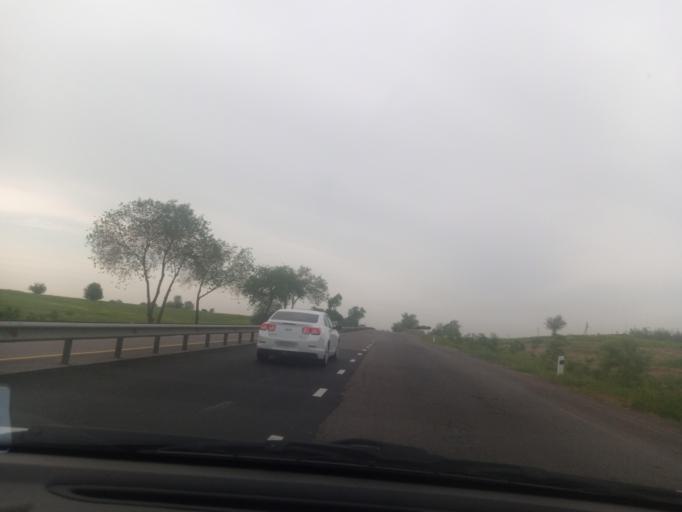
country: UZ
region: Toshkent
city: Tuytepa
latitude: 41.1109
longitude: 69.4486
